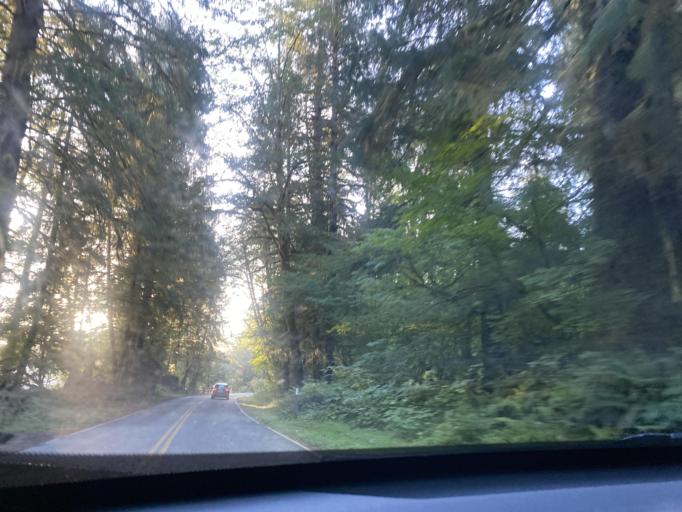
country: US
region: Washington
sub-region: Clallam County
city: Forks
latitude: 47.8183
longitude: -124.1732
